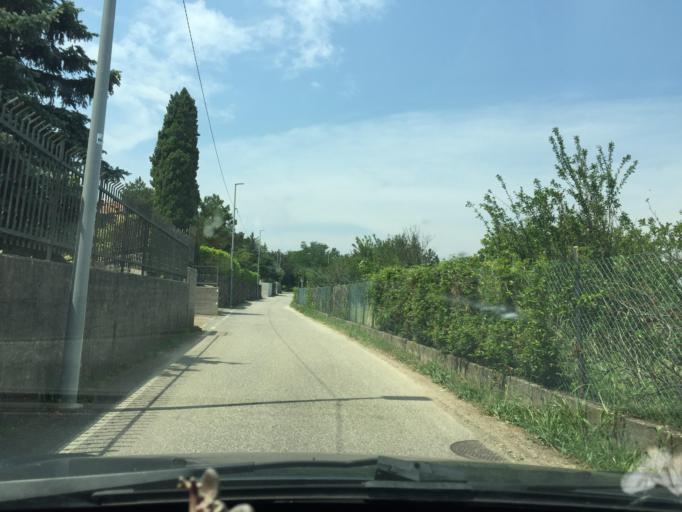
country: IT
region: Friuli Venezia Giulia
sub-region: Provincia di Trieste
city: Domio
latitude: 45.5930
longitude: 13.8347
